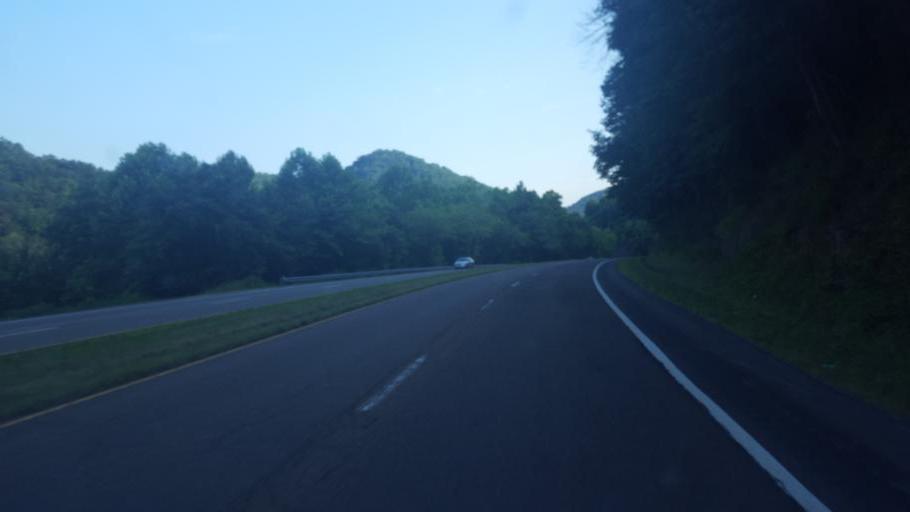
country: US
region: Tennessee
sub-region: Hawkins County
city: Mount Carmel
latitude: 36.6928
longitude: -82.7533
